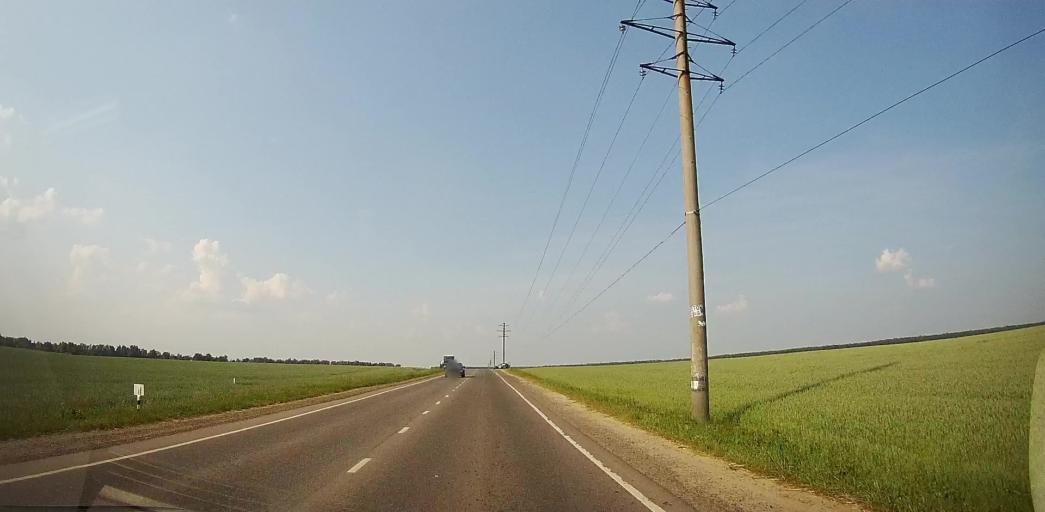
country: RU
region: Moskovskaya
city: Barybino
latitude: 55.2533
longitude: 37.9186
